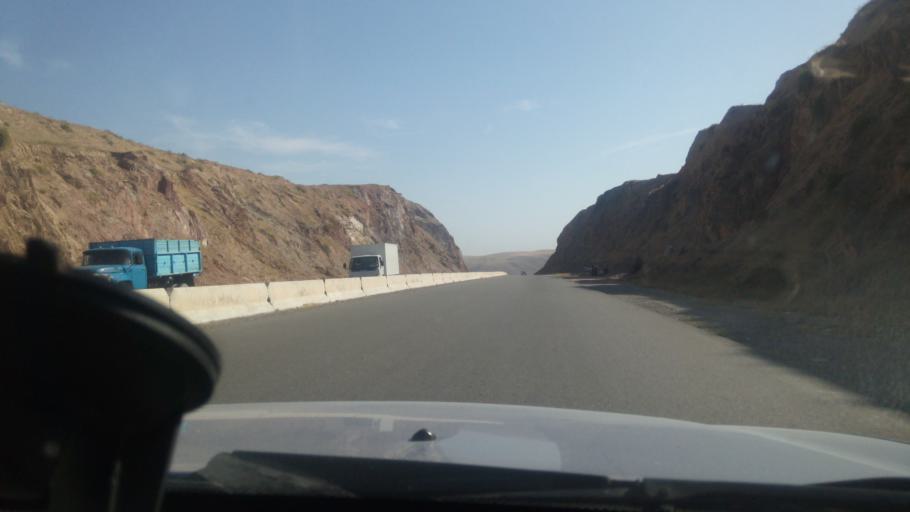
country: UZ
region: Jizzax
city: Jizzax
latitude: 40.0483
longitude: 67.6776
